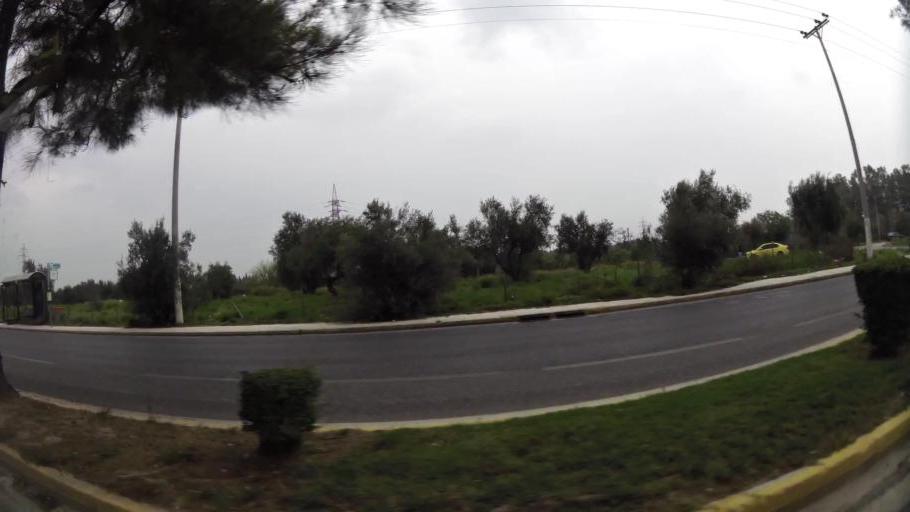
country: GR
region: Attica
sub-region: Nomarchia Athinas
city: Agioi Anargyroi
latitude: 38.0388
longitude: 23.7162
